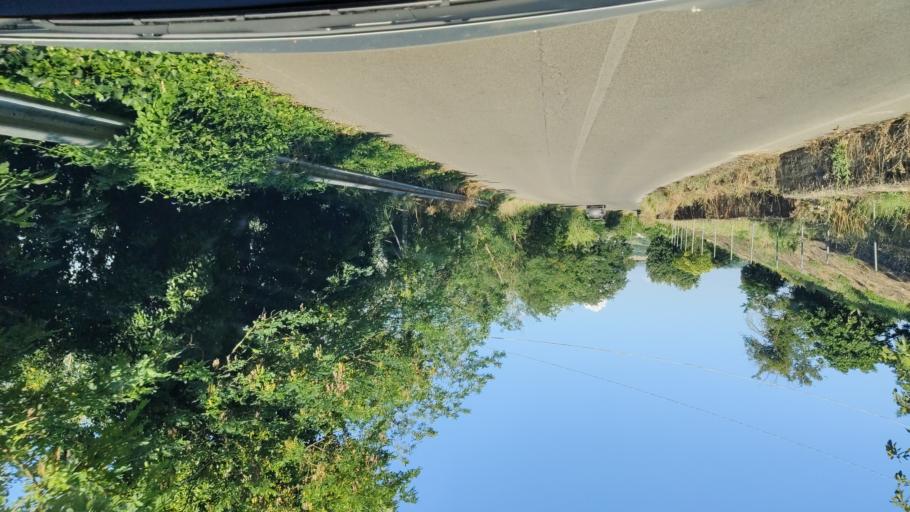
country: IT
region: Latium
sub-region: Provincia di Viterbo
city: Orte
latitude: 42.4693
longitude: 12.3772
